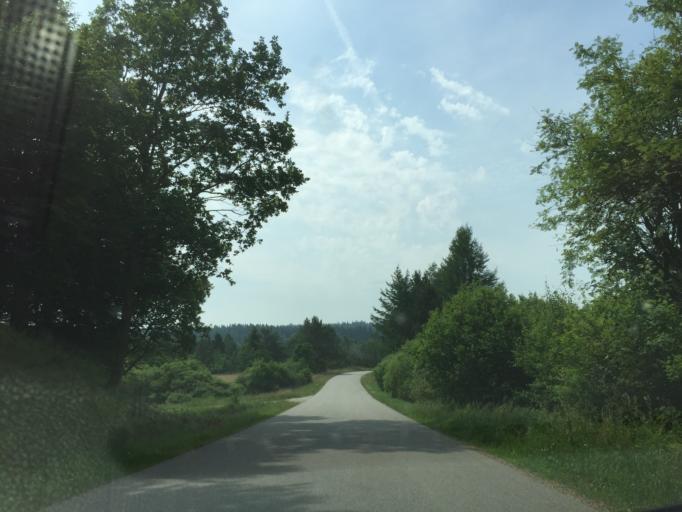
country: DK
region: Central Jutland
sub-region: Silkeborg Kommune
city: Virklund
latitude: 56.0600
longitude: 9.4662
